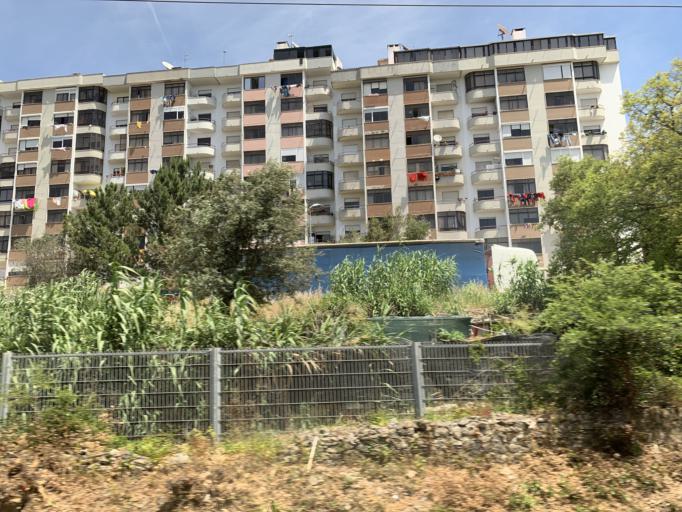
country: PT
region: Lisbon
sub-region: Sintra
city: Rio de Mouro
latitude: 38.7823
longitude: -9.3139
